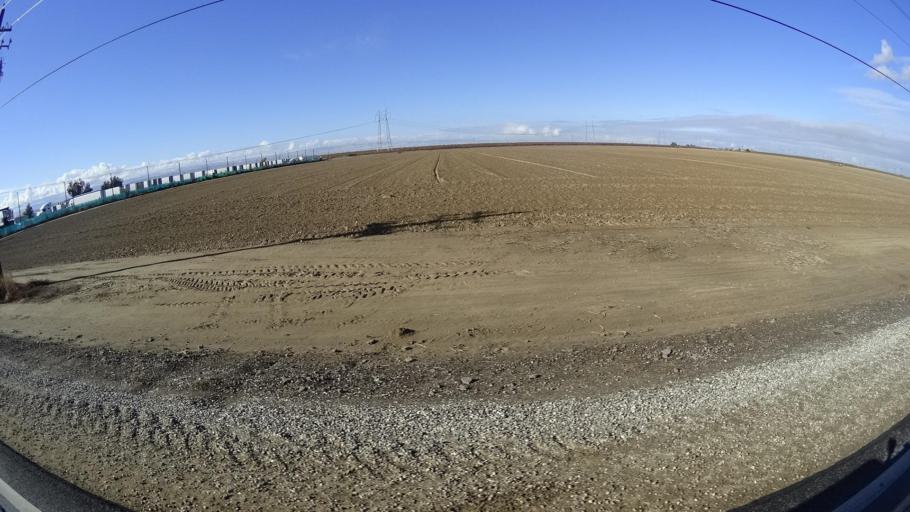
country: US
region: California
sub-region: Kern County
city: Rosedale
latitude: 35.3713
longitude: -119.2514
